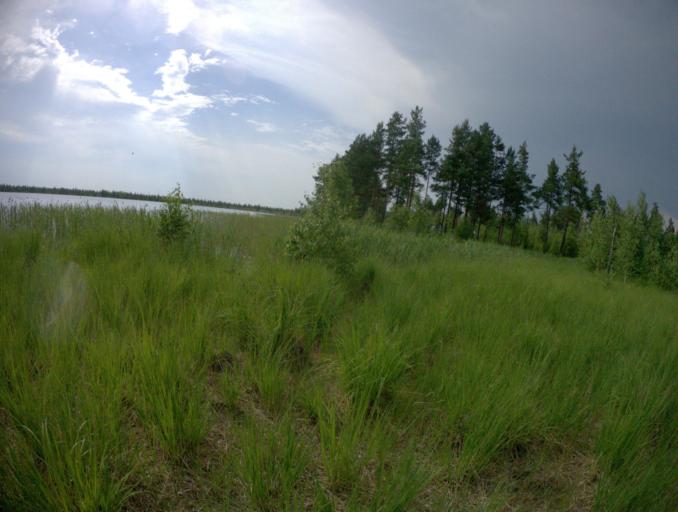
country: RU
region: Ivanovo
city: Talitsy
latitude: 56.4311
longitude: 42.3285
